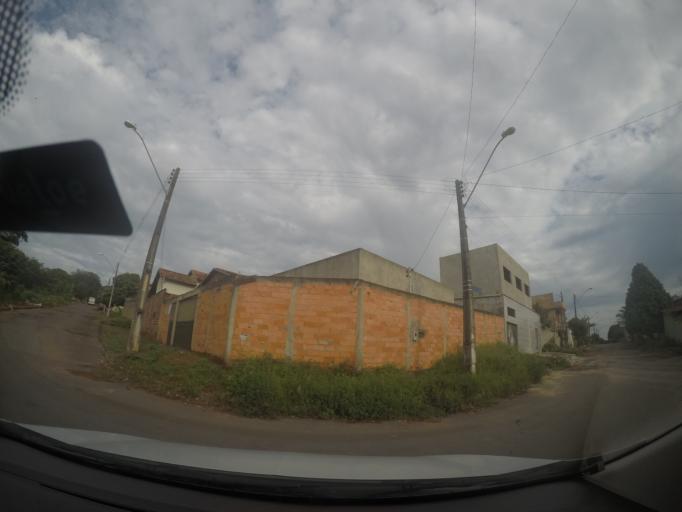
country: BR
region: Goias
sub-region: Goiania
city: Goiania
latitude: -16.6883
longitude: -49.1979
